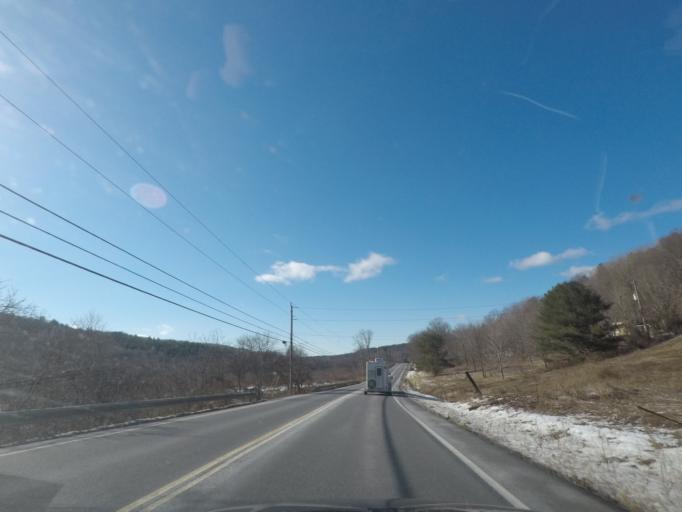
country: US
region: New York
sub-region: Columbia County
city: Chatham
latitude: 42.4173
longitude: -73.4874
